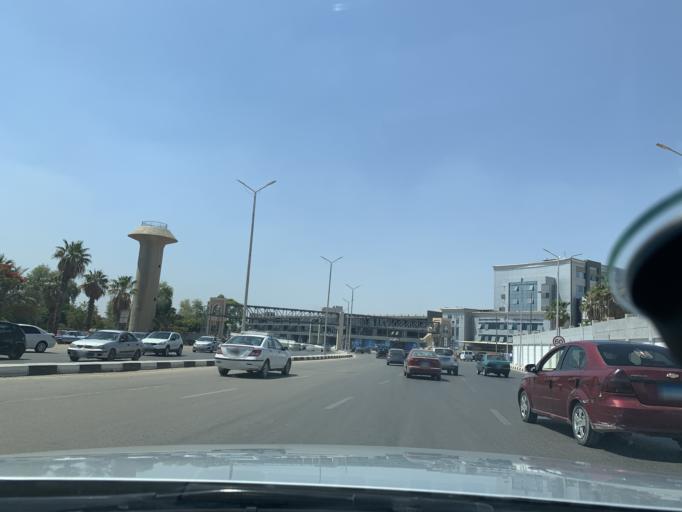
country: EG
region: Muhafazat al Qahirah
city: Cairo
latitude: 30.0905
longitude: 31.3487
